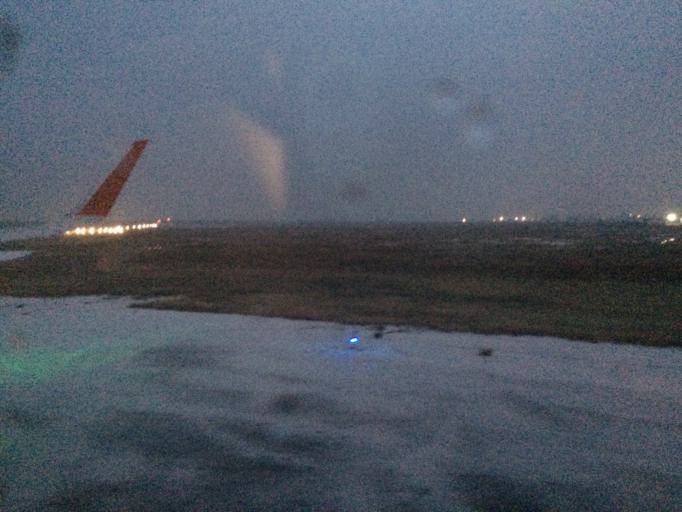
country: RU
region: Novosibirsk
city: Ob'
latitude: 55.0145
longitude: 82.6779
